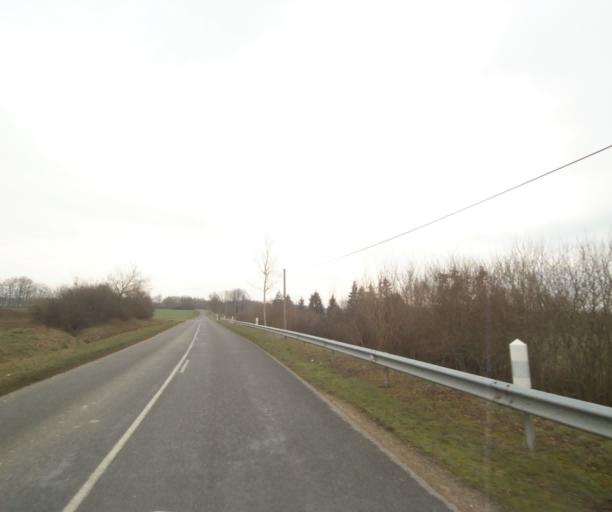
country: FR
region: Champagne-Ardenne
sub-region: Departement de la Marne
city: Pargny-sur-Saulx
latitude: 48.7431
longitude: 4.8492
